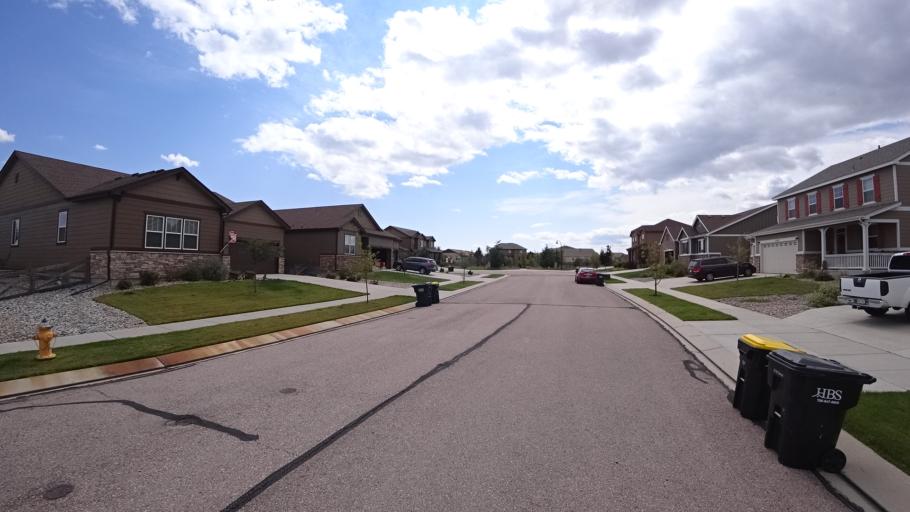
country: US
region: Colorado
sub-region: El Paso County
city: Cimarron Hills
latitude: 38.9351
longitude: -104.6776
